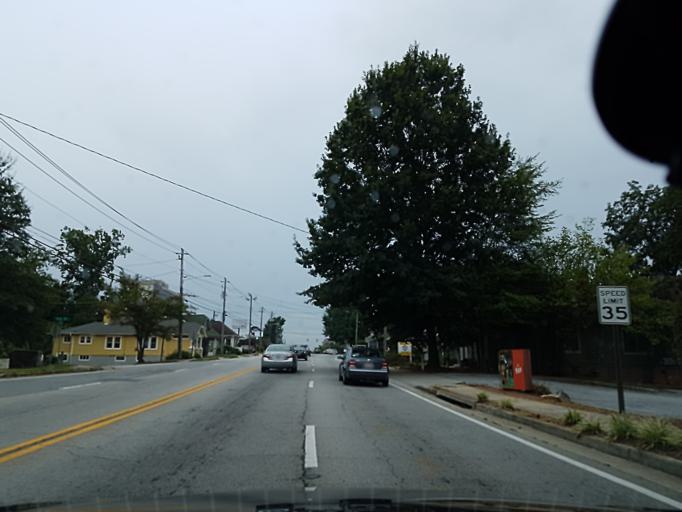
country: US
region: Georgia
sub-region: DeKalb County
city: Decatur
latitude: 33.7803
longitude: -84.2948
